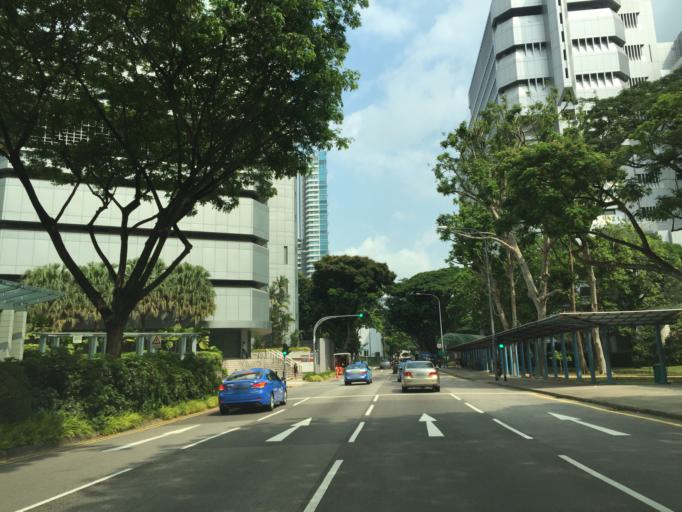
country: SG
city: Singapore
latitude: 1.2995
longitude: 103.8385
